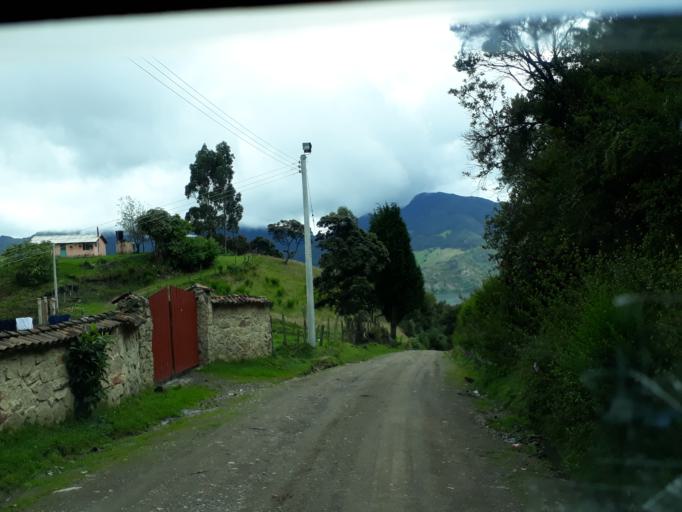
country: CO
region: Cundinamarca
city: Cogua
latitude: 5.1544
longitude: -73.9821
